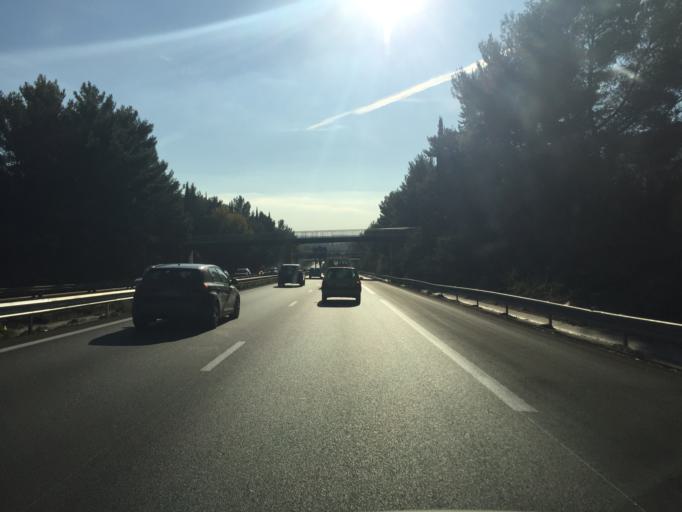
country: FR
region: Provence-Alpes-Cote d'Azur
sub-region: Departement des Bouches-du-Rhone
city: Aix-en-Provence
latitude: 43.5348
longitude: 5.4308
